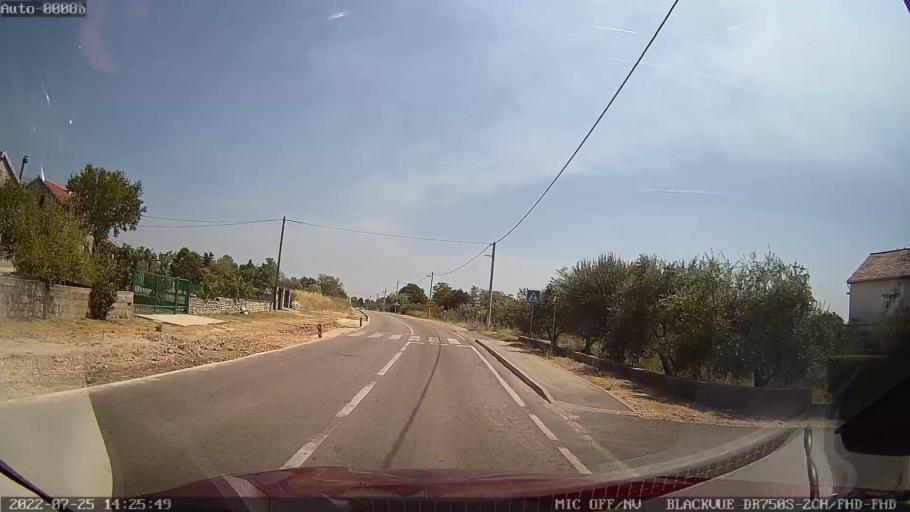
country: HR
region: Zadarska
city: Policnik
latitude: 44.1425
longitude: 15.3339
